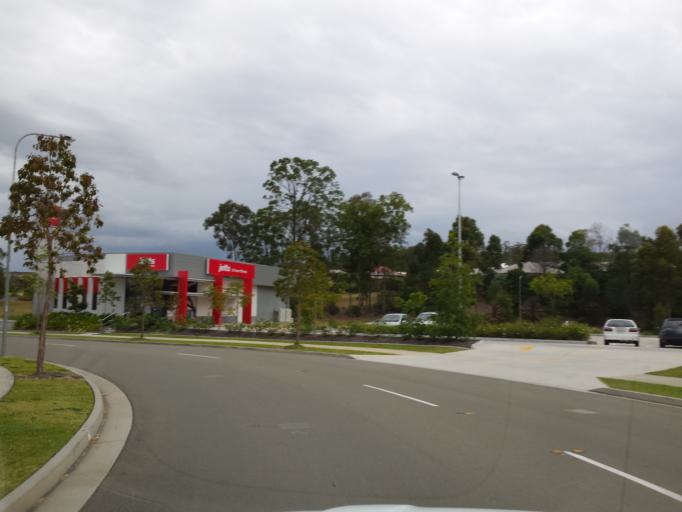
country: AU
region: Queensland
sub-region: Gold Coast
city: Oxenford
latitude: -27.8503
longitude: 153.2972
